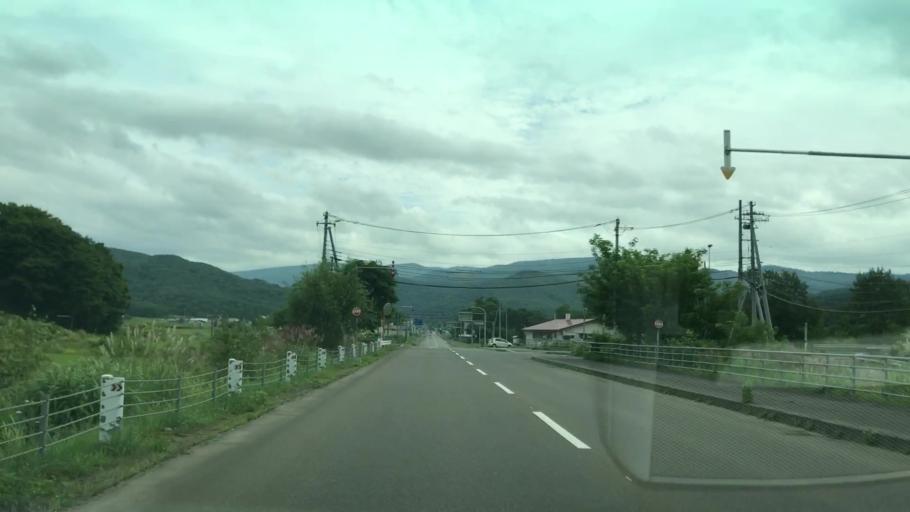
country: JP
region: Hokkaido
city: Yoichi
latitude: 43.0510
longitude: 140.8239
